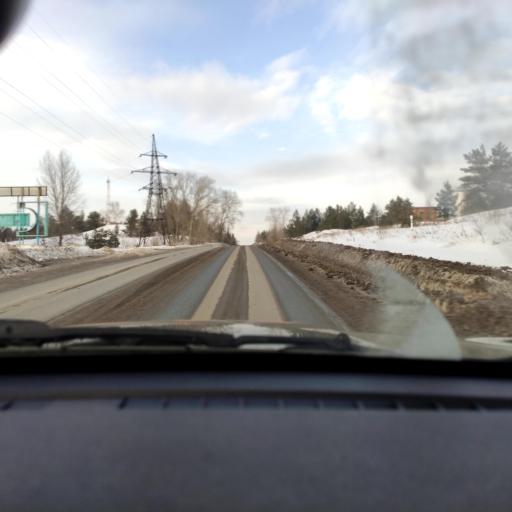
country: RU
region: Samara
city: Pribrezhnyy
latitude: 53.4947
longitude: 49.8479
